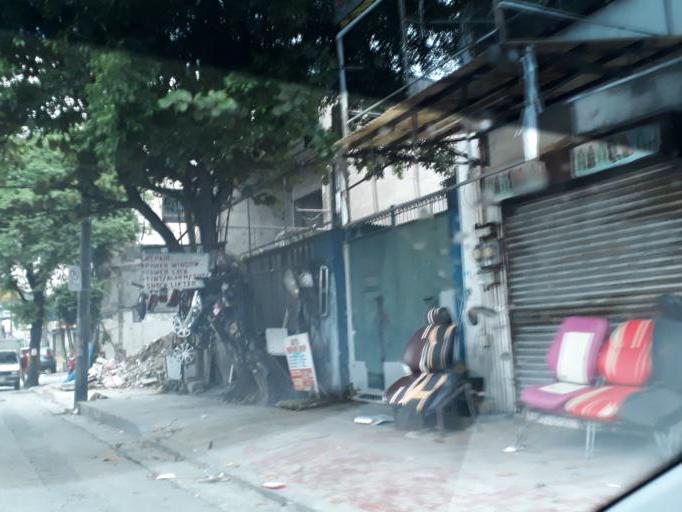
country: PH
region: Calabarzon
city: Del Monte
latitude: 14.6359
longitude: 121.0013
